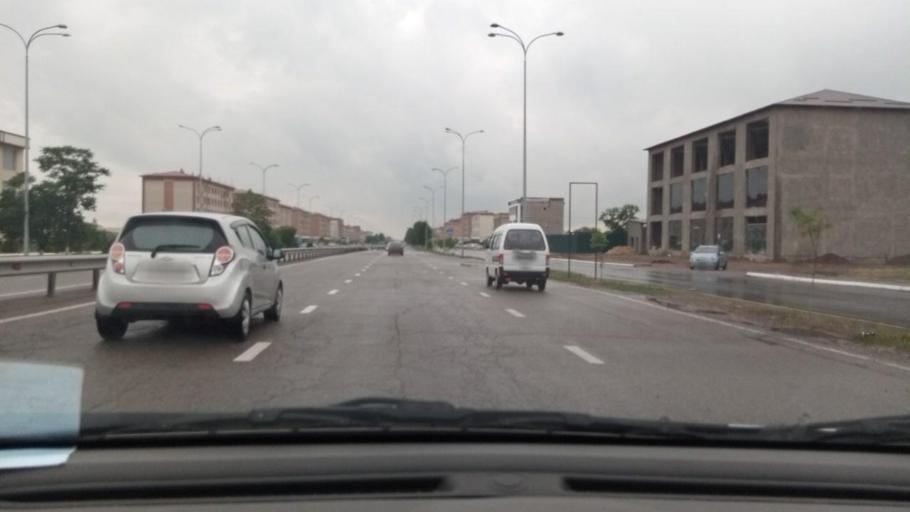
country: UZ
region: Toshkent
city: Ohangaron
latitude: 40.9054
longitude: 69.6356
